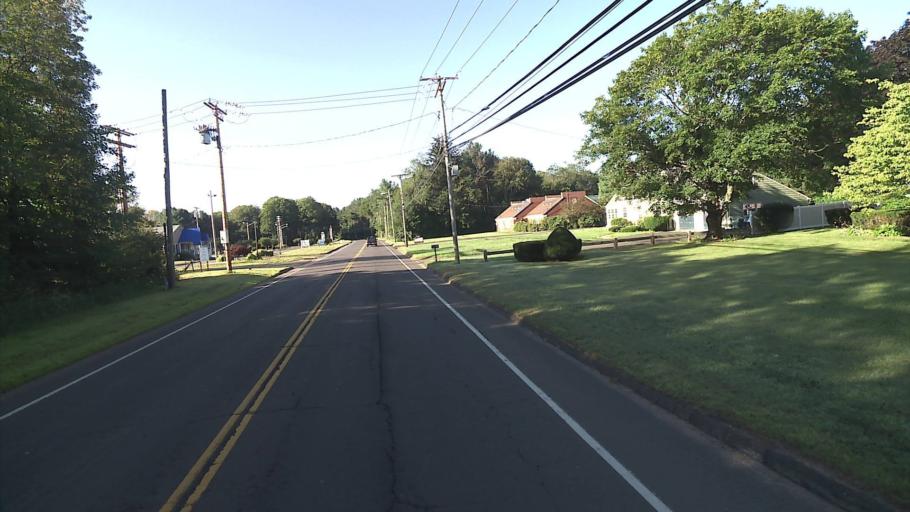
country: US
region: Connecticut
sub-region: New Haven County
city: Hamden
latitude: 41.4441
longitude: -72.9107
